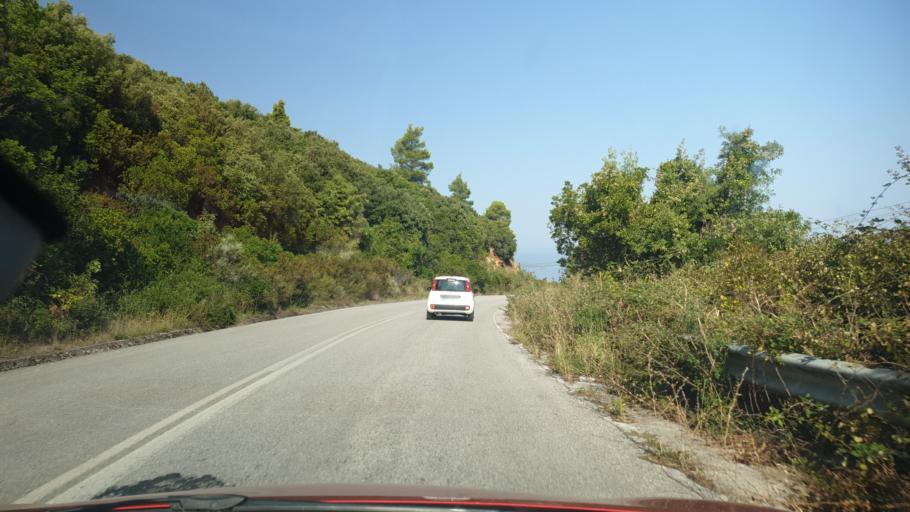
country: GR
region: Central Macedonia
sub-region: Nomos Chalkidikis
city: Neos Marmaras
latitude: 40.1671
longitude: 23.8634
